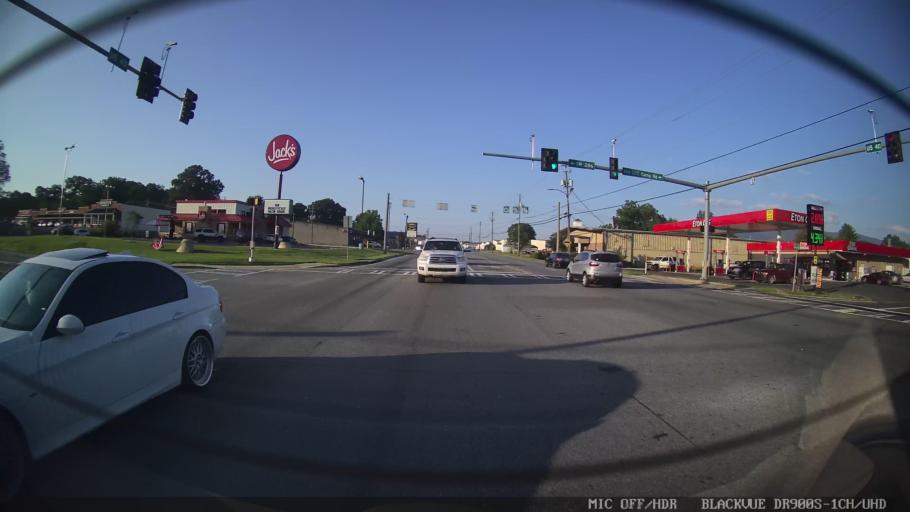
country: US
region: Georgia
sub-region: Murray County
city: Chatsworth
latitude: 34.8246
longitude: -84.7632
